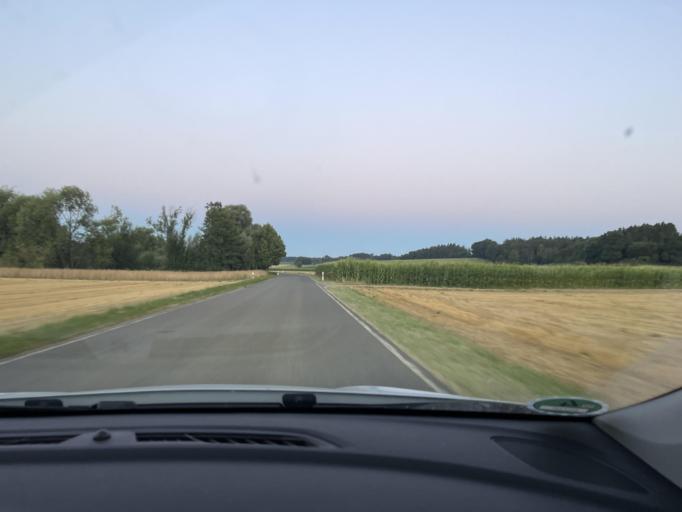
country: DE
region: Bavaria
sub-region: Swabia
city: Aichach
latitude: 48.4410
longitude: 11.1029
